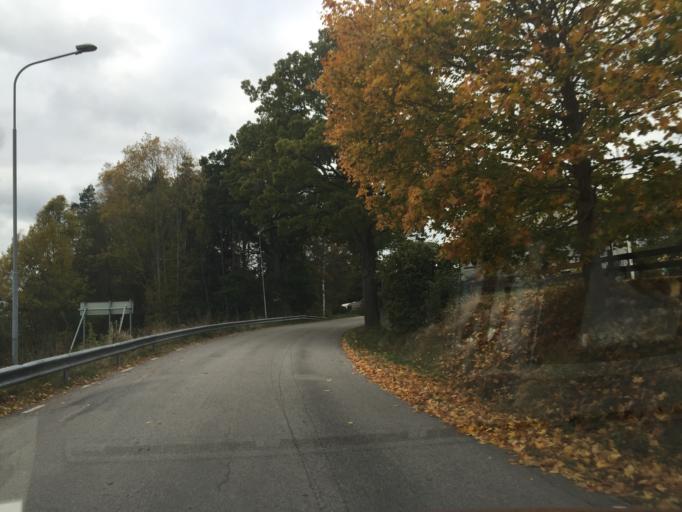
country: SE
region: OEstergoetland
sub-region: Linkopings Kommun
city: Ljungsbro
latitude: 58.7877
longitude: 15.4949
